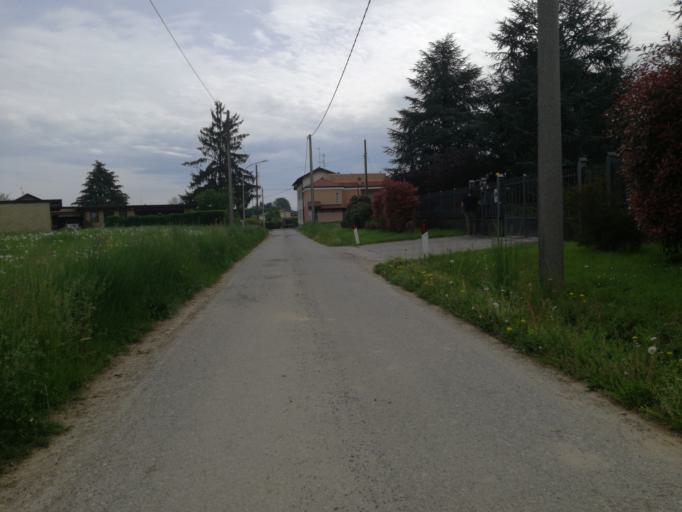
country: IT
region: Lombardy
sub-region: Provincia di Monza e Brianza
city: Mezzago
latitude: 45.6496
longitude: 9.4538
